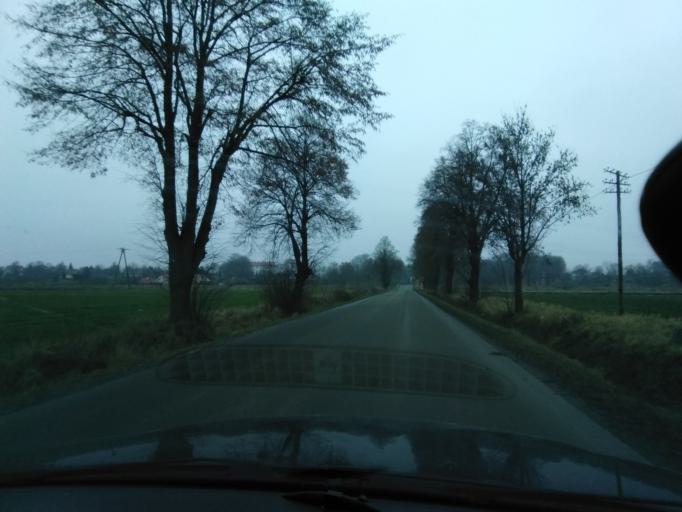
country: PL
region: Subcarpathian Voivodeship
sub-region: Powiat przeworski
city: Urzejowice
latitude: 50.0095
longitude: 22.4704
